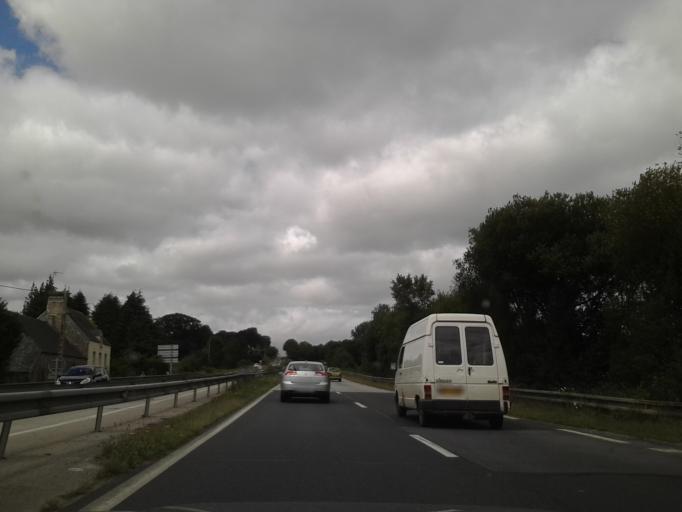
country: FR
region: Lower Normandy
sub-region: Departement de la Manche
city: Brix
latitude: 49.5572
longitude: -1.5646
